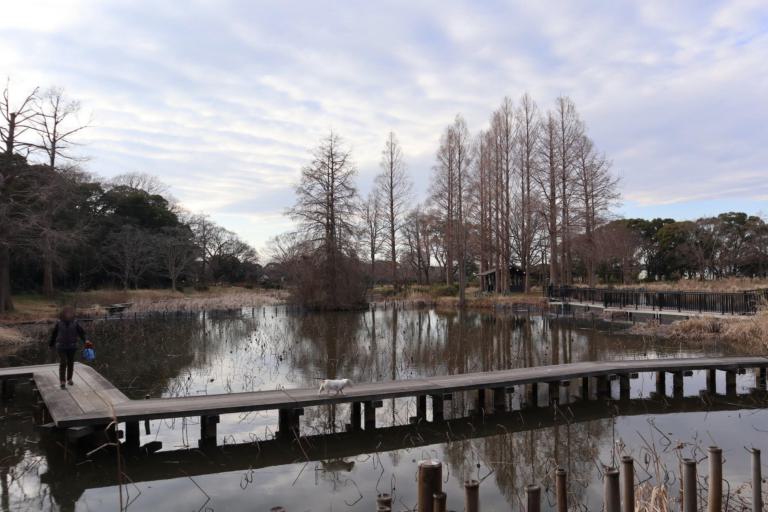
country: JP
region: Chiba
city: Matsudo
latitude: 35.7955
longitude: 139.8739
